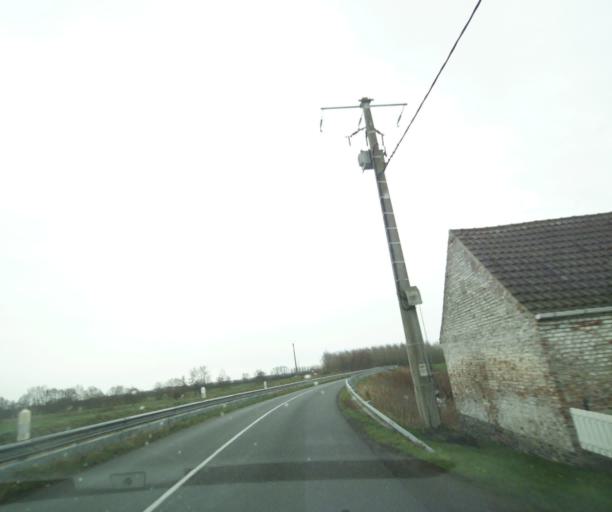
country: FR
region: Nord-Pas-de-Calais
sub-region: Departement du Nord
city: Crespin
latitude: 50.4355
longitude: 3.6443
